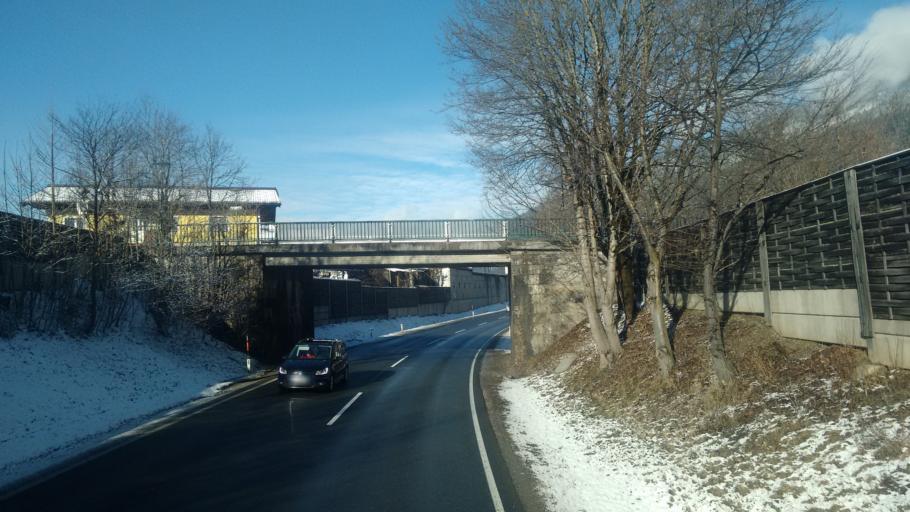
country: AT
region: Salzburg
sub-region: Politischer Bezirk Sankt Johann im Pongau
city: Radstadt
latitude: 47.3860
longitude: 13.4612
